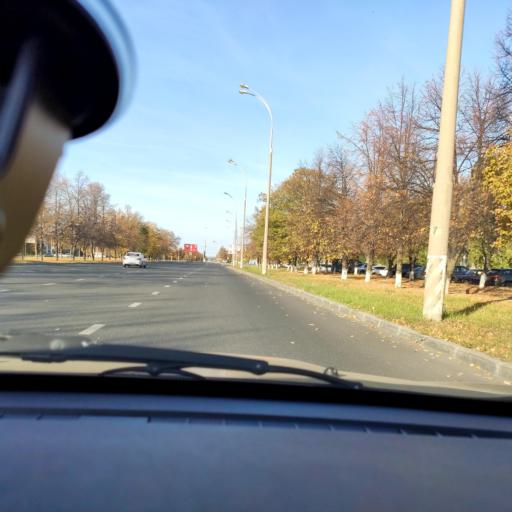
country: RU
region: Samara
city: Tol'yatti
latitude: 53.5184
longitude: 49.2989
